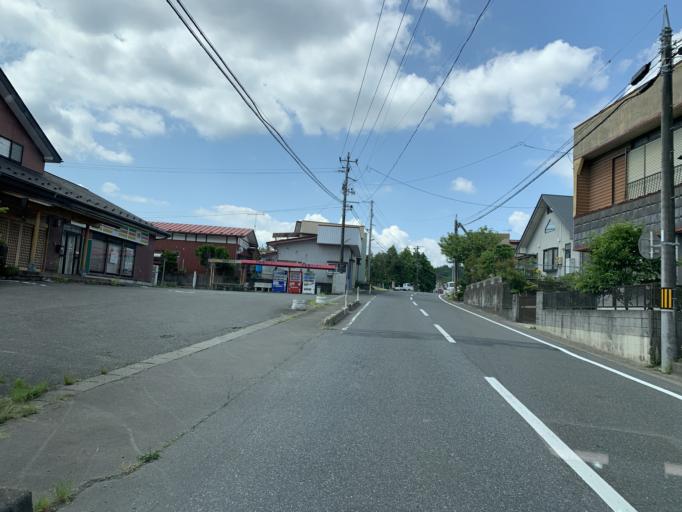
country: JP
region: Miyagi
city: Furukawa
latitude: 38.7667
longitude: 140.9626
